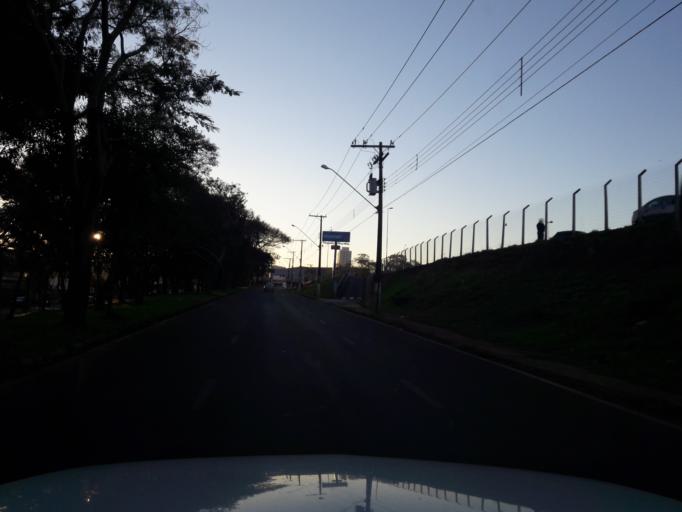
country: BR
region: Sao Paulo
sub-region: Moji-Guacu
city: Mogi-Gaucu
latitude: -22.3598
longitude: -46.9351
